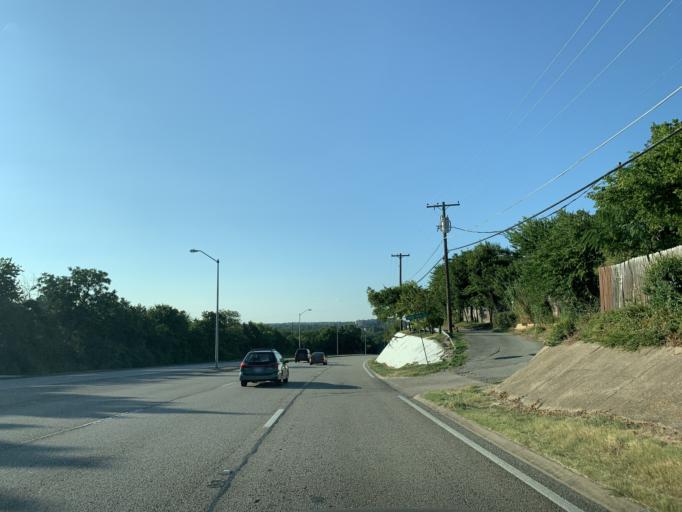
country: US
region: Texas
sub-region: Dallas County
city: Hutchins
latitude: 32.6732
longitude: -96.7843
